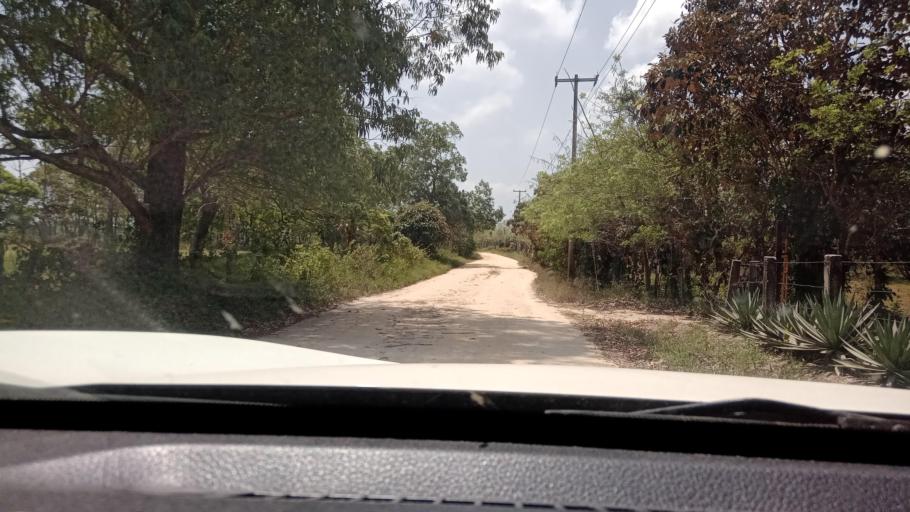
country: MX
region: Veracruz
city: Las Choapas
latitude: 17.9420
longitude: -94.1228
